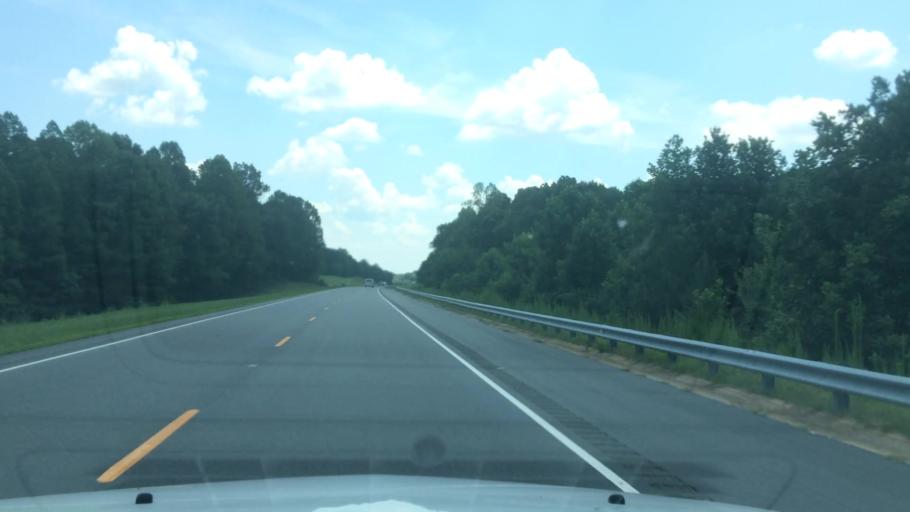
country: US
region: North Carolina
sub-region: Alexander County
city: Stony Point
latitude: 35.8749
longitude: -81.0679
